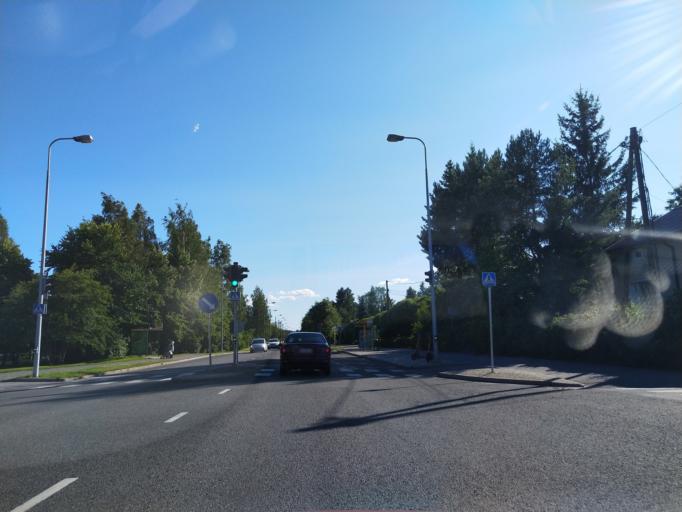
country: FI
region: Varsinais-Suomi
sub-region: Turku
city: Kaarina
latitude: 60.4445
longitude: 22.3258
